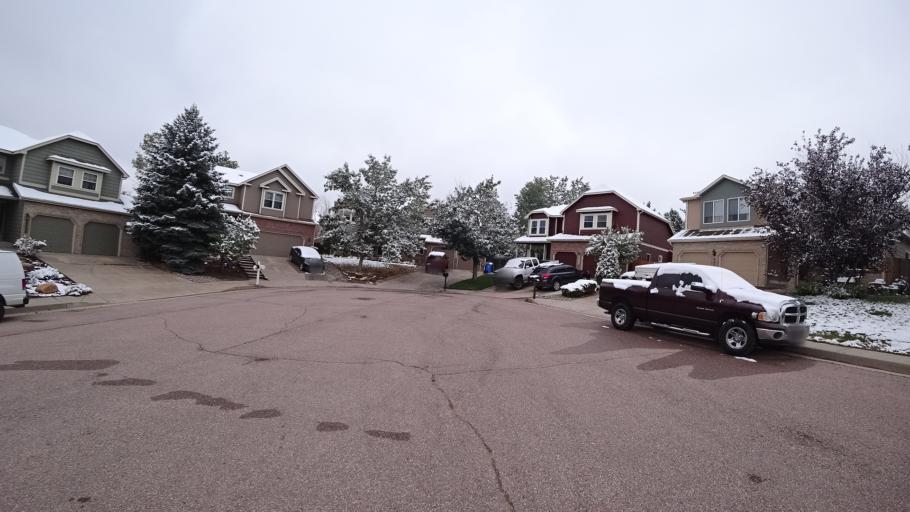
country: US
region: Colorado
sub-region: El Paso County
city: Colorado Springs
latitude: 38.9238
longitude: -104.7822
